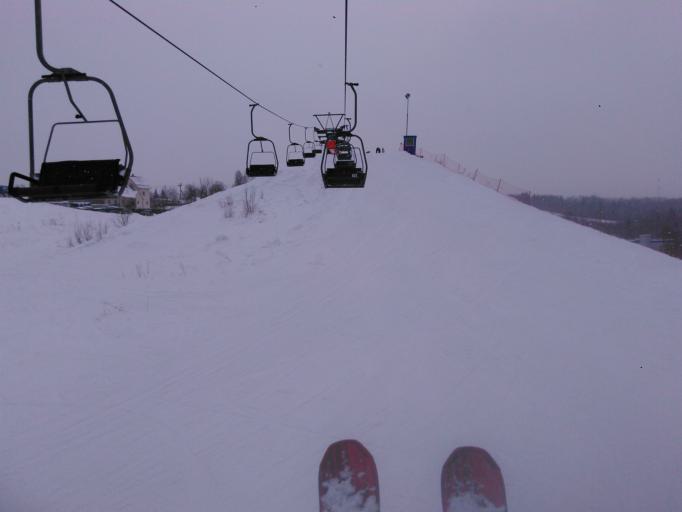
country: RU
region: Moskovskaya
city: Yakhroma
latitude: 56.2514
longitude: 37.4394
